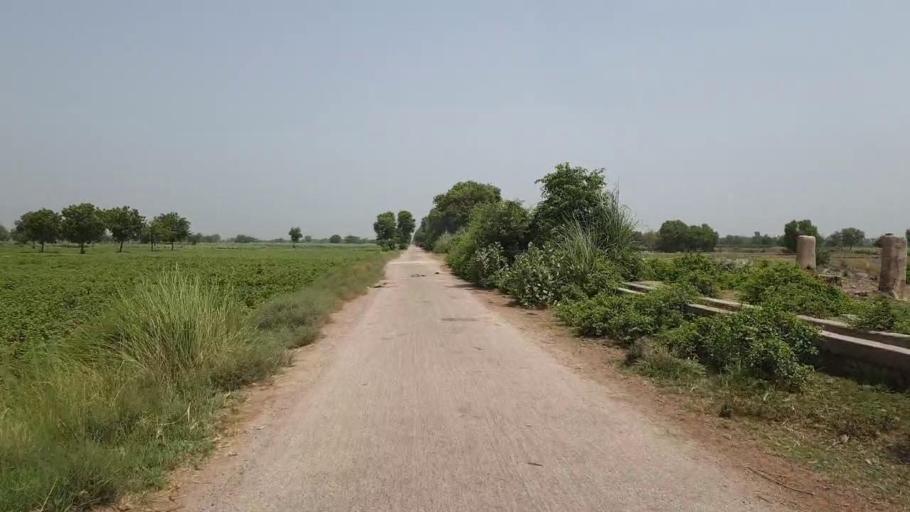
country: PK
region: Sindh
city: Nawabshah
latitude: 26.2895
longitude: 68.3089
